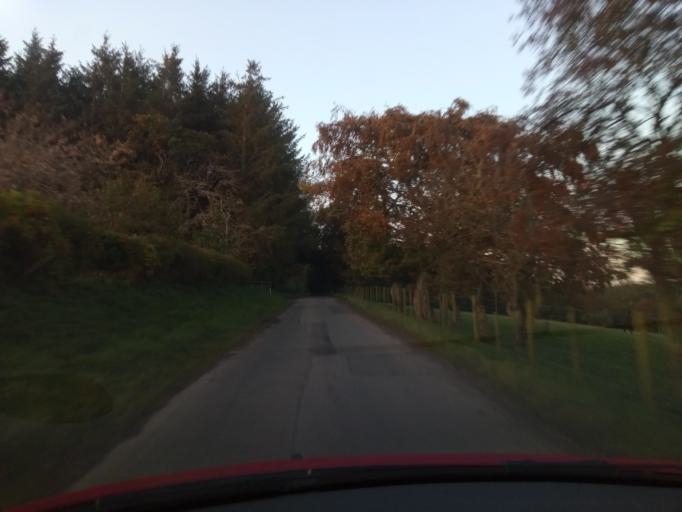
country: GB
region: Scotland
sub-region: Fife
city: Pathhead
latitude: 55.7939
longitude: -2.8896
